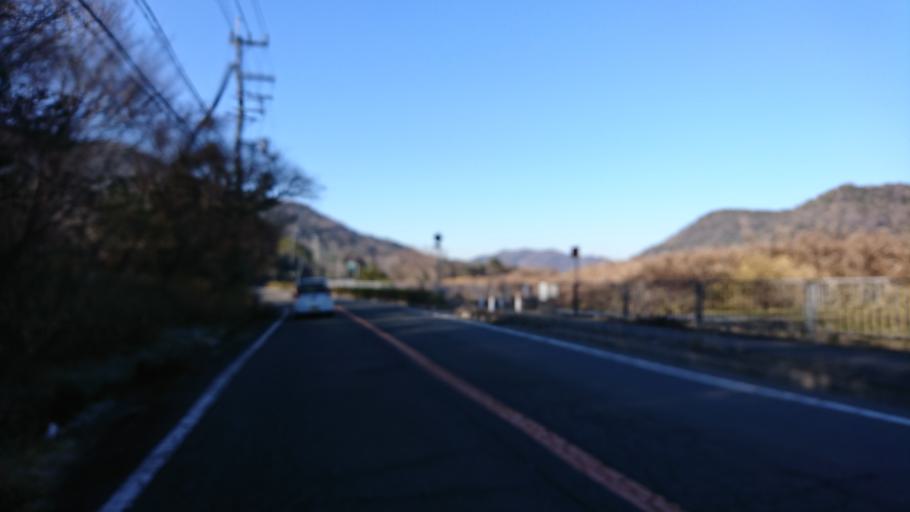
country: JP
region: Hyogo
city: Kakogawacho-honmachi
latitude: 34.8406
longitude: 134.8528
